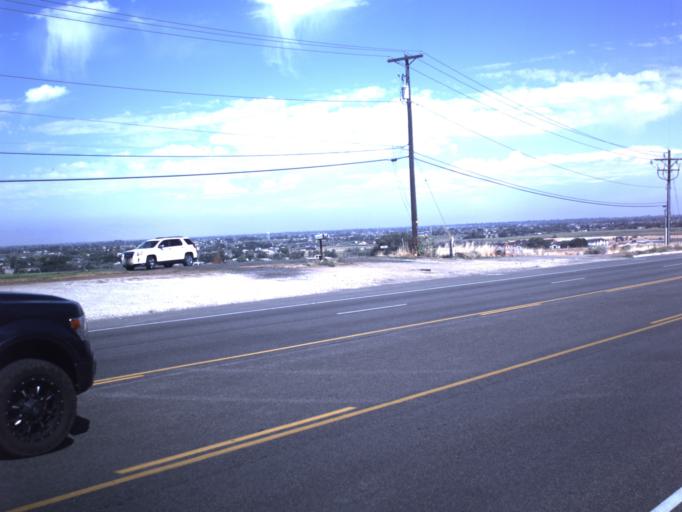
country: US
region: Utah
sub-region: Weber County
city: West Haven
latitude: 41.1964
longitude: -112.0257
